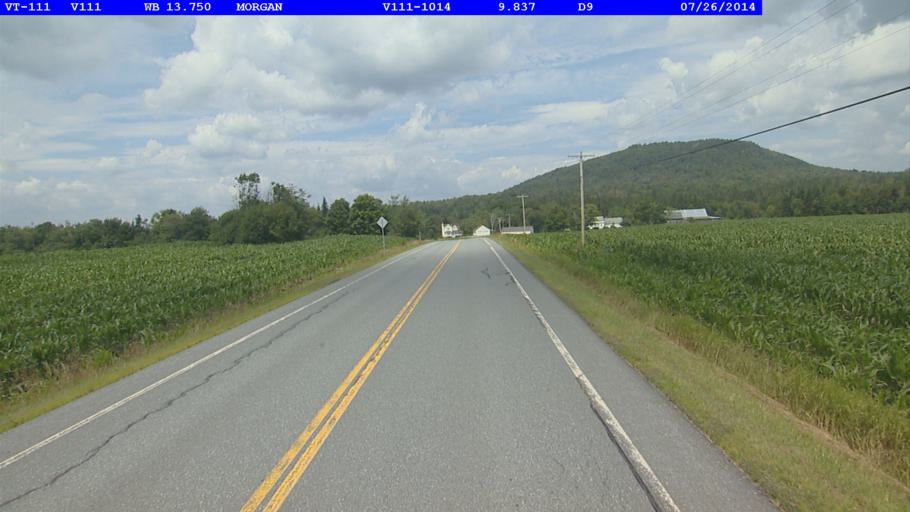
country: US
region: Vermont
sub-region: Orleans County
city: Newport
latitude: 44.8596
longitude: -71.9268
